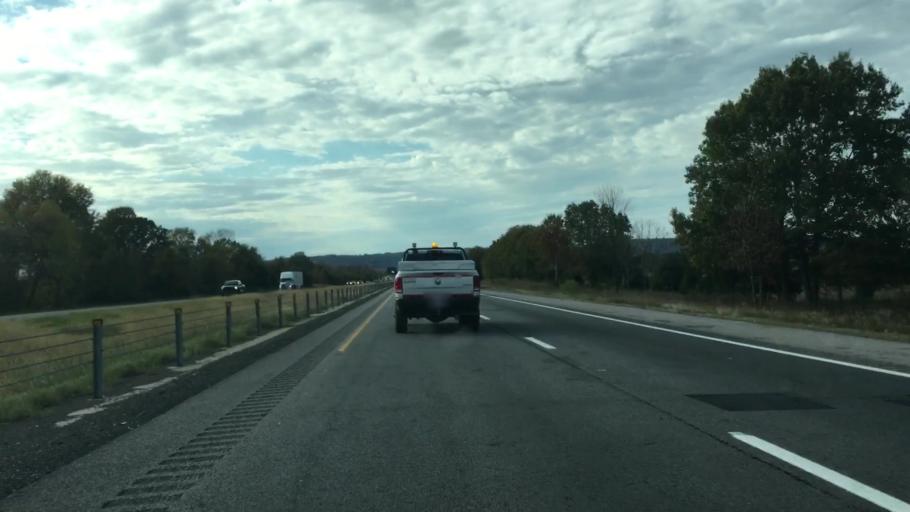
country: US
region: Arkansas
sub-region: Pope County
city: Atkins
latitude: 35.2484
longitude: -92.8760
